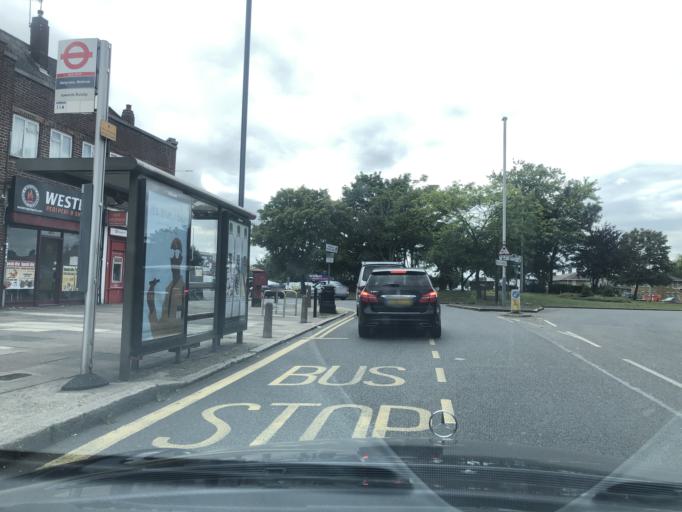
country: GB
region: England
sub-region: Greater London
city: Northolt
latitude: 51.5597
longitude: -0.3796
